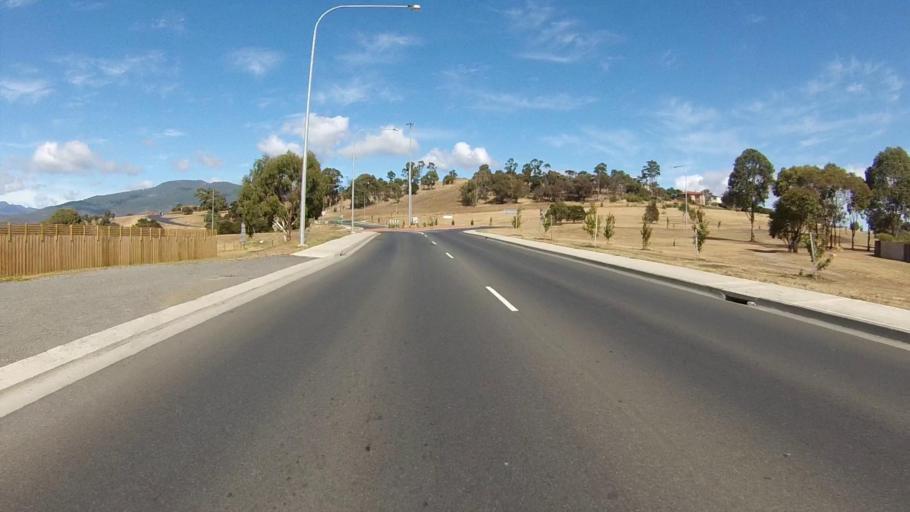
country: AU
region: Tasmania
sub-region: Brighton
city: Old Beach
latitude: -42.7509
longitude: 147.2740
